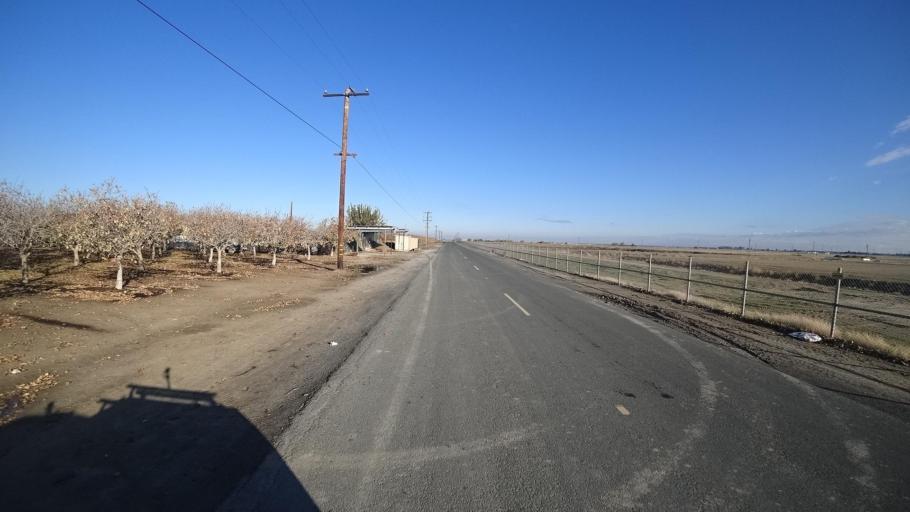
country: US
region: California
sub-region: Kern County
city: Delano
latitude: 35.7720
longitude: -119.3297
